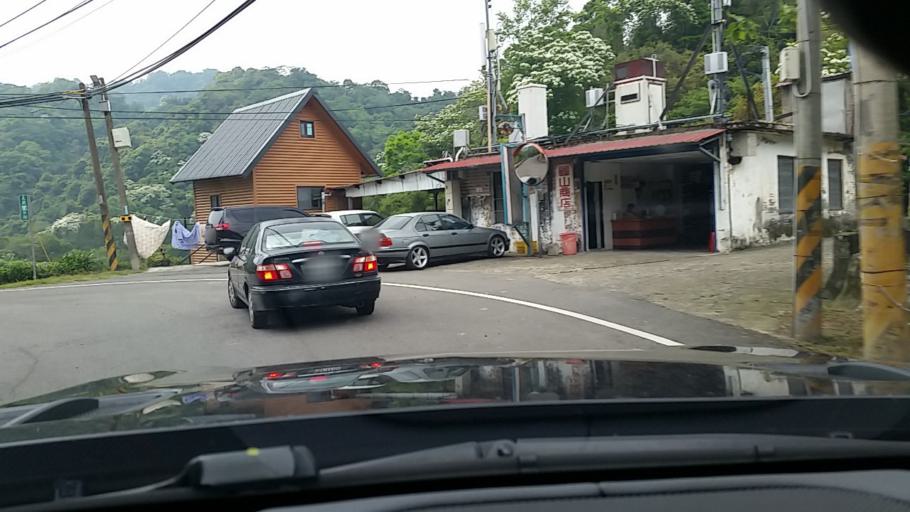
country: TW
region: Taiwan
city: Daxi
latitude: 24.7990
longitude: 121.2845
